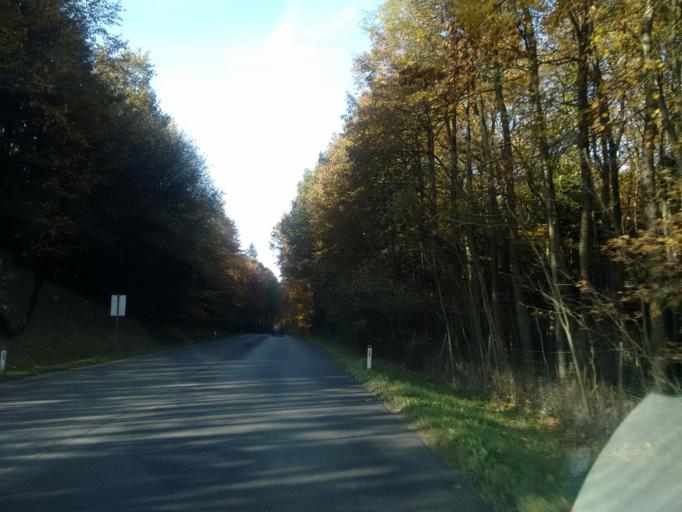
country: AT
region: Upper Austria
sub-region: Politischer Bezirk Vocklabruck
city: Wolfsegg am Hausruck
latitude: 48.1987
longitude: 13.6257
